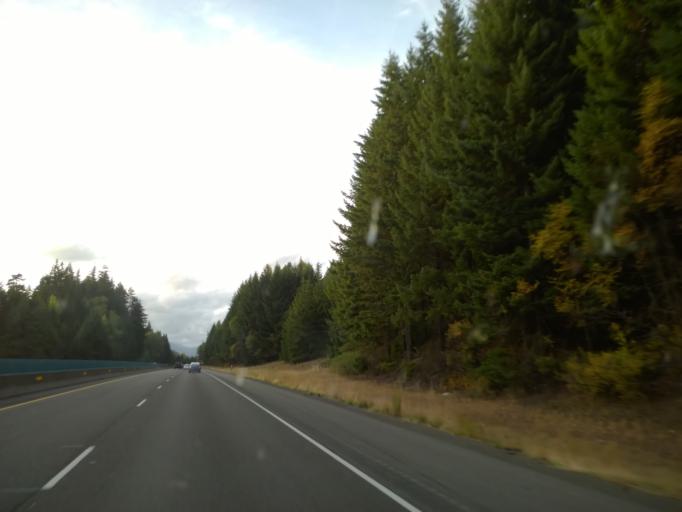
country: US
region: Washington
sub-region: Kittitas County
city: Cle Elum
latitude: 47.2733
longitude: -121.2729
